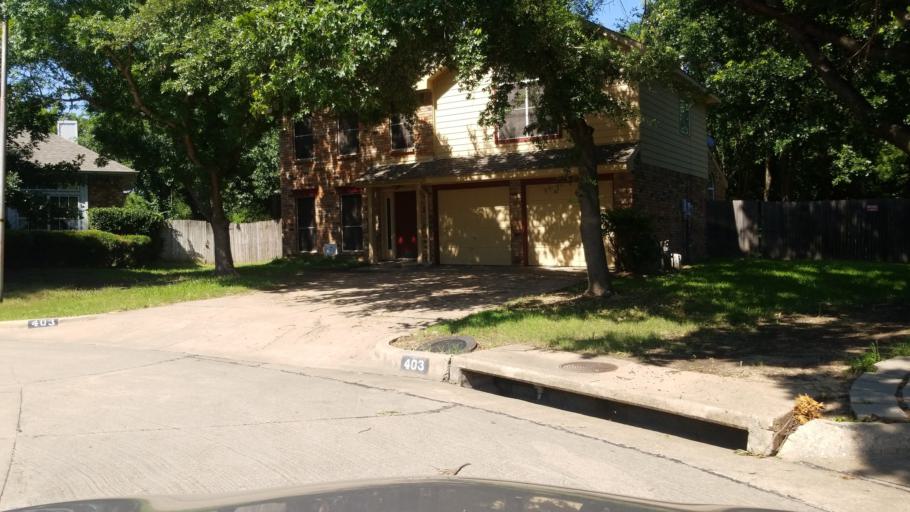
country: US
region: Texas
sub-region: Dallas County
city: Grand Prairie
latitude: 32.6922
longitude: -97.0105
